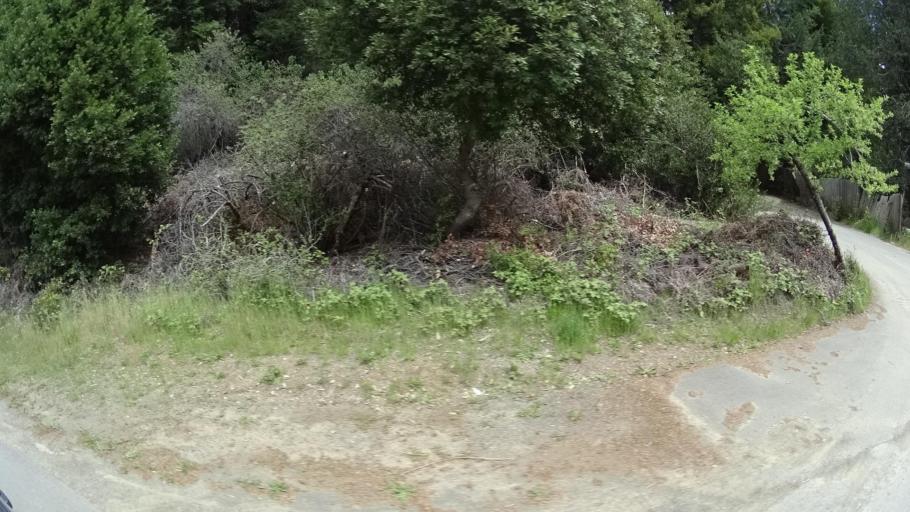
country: US
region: California
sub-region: Humboldt County
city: Redway
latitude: 40.0240
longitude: -123.9435
